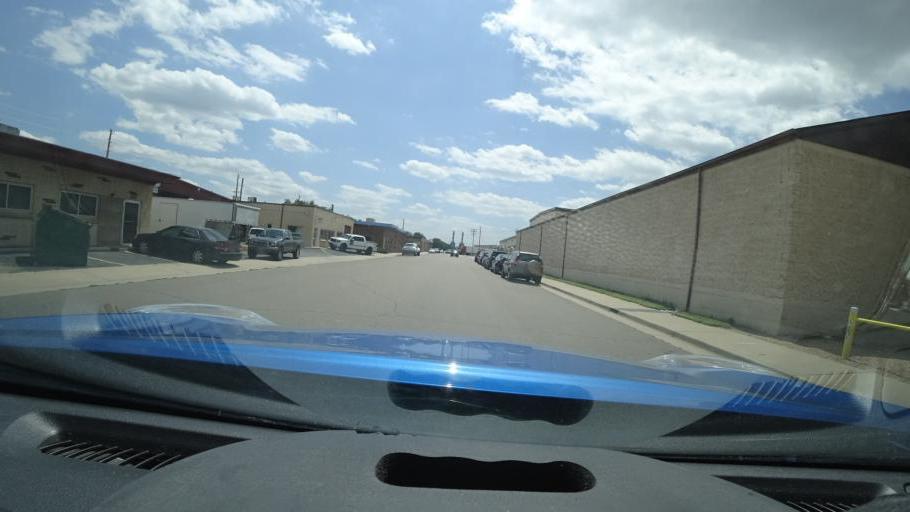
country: US
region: Colorado
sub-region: Arapahoe County
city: Englewood
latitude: 39.6764
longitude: -105.0018
